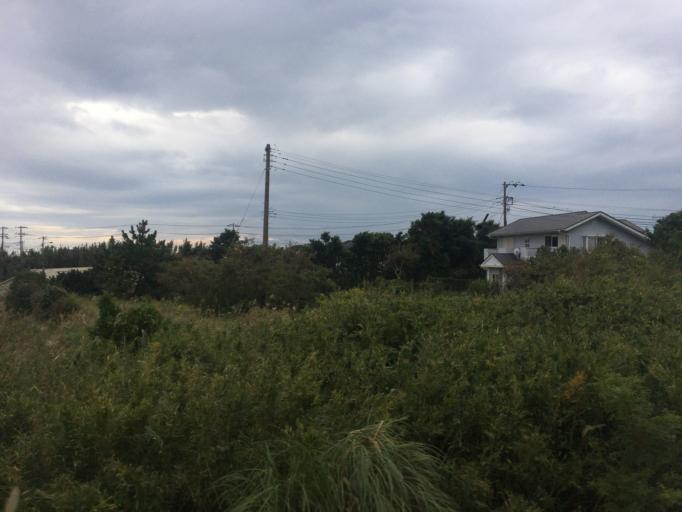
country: JP
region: Chiba
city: Futtsu
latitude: 35.1443
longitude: 139.8361
